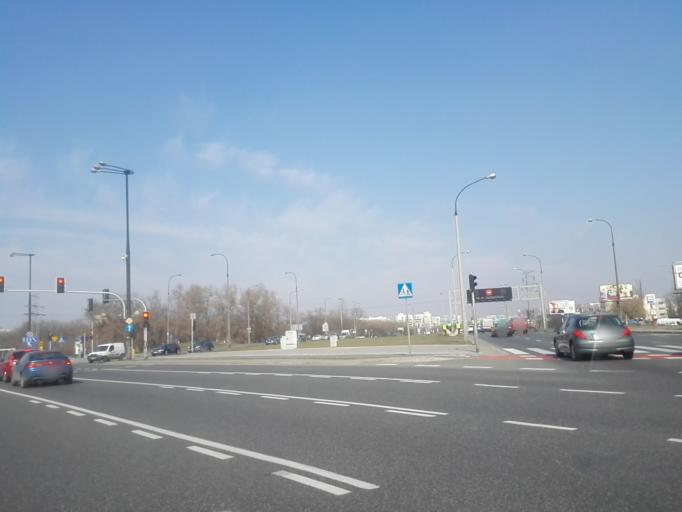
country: PL
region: Masovian Voivodeship
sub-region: Warszawa
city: Mokotow
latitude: 52.1901
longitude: 21.0470
